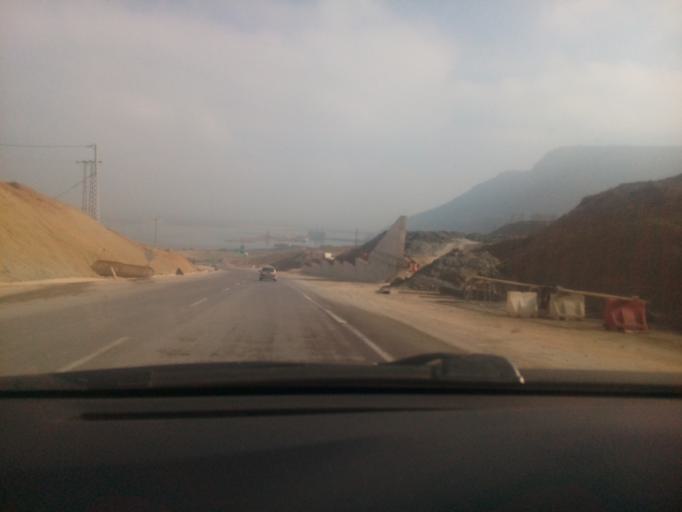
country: DZ
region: Oran
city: Mers el Kebir
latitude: 35.7132
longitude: -0.6974
